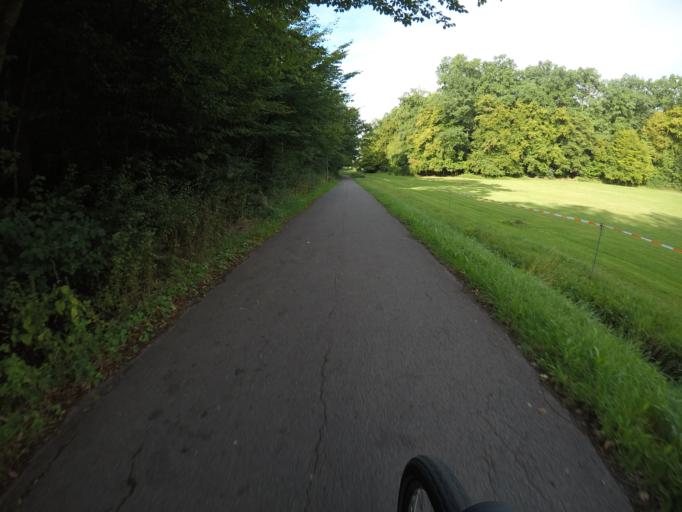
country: DE
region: Baden-Wuerttemberg
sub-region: Regierungsbezirk Stuttgart
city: Magstadt
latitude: 48.7248
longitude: 8.9956
